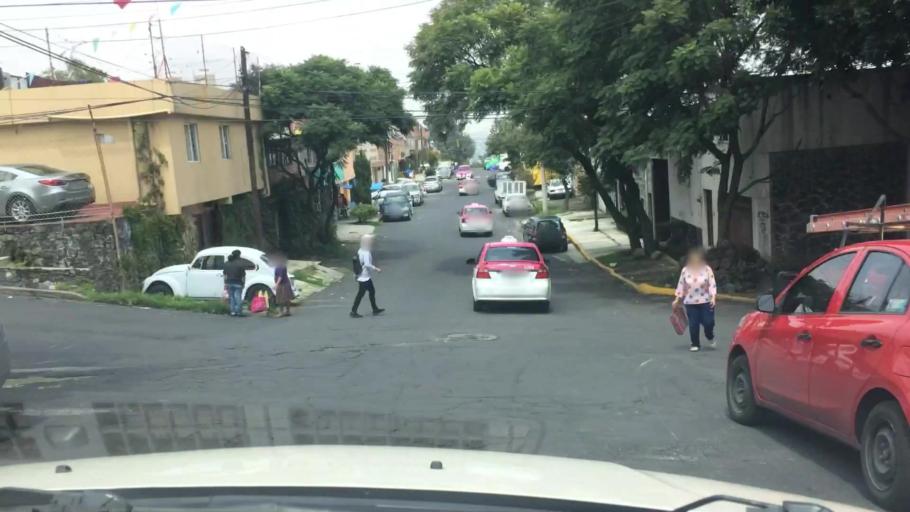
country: MX
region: Mexico City
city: Magdalena Contreras
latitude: 19.2973
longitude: -99.2255
